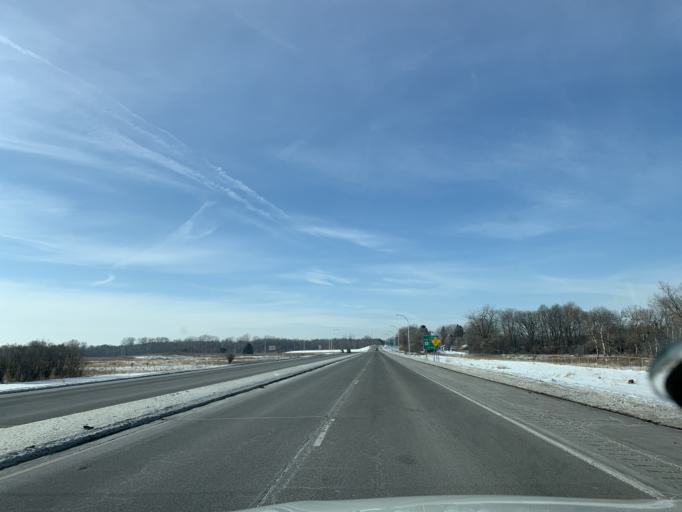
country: US
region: Minnesota
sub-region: Washington County
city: Forest Lake
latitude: 45.2898
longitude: -92.9954
